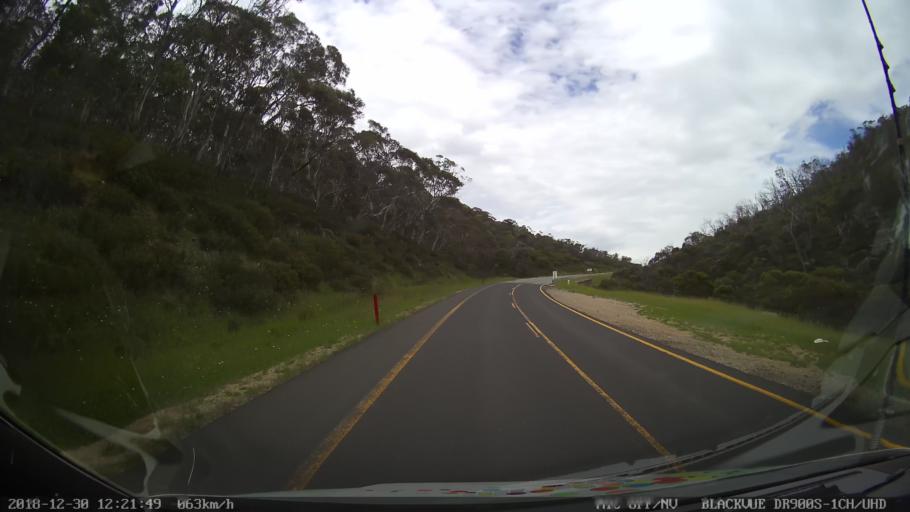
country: AU
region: New South Wales
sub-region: Snowy River
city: Jindabyne
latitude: -36.3547
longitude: 148.5152
